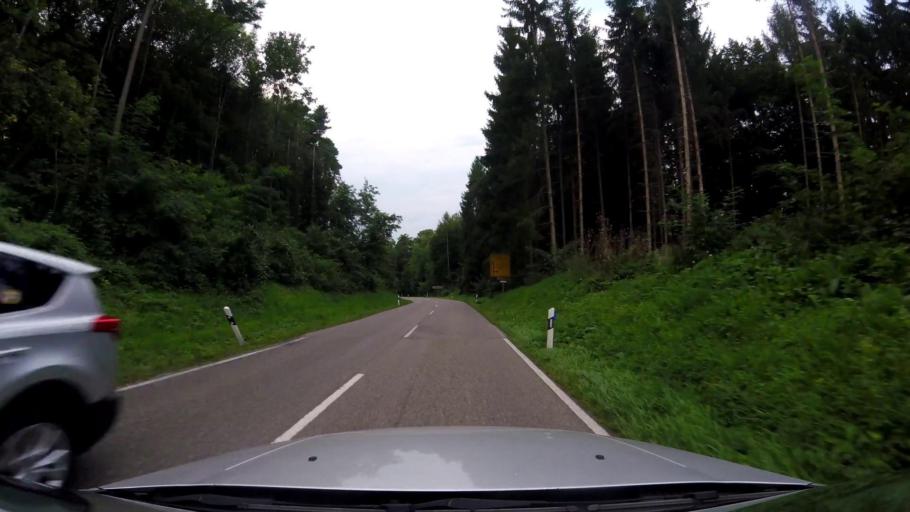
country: DE
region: Baden-Wuerttemberg
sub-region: Regierungsbezirk Stuttgart
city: Allmersbach im Tal
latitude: 48.8994
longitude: 9.4792
